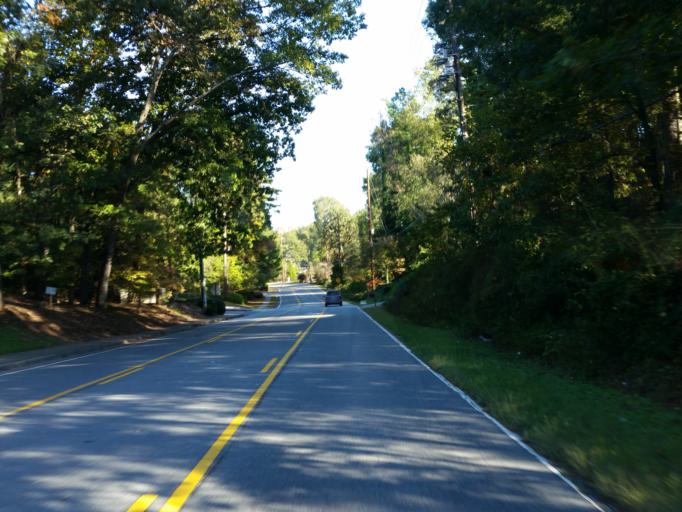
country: US
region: Georgia
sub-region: Fulton County
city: Roswell
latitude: 33.9948
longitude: -84.4075
